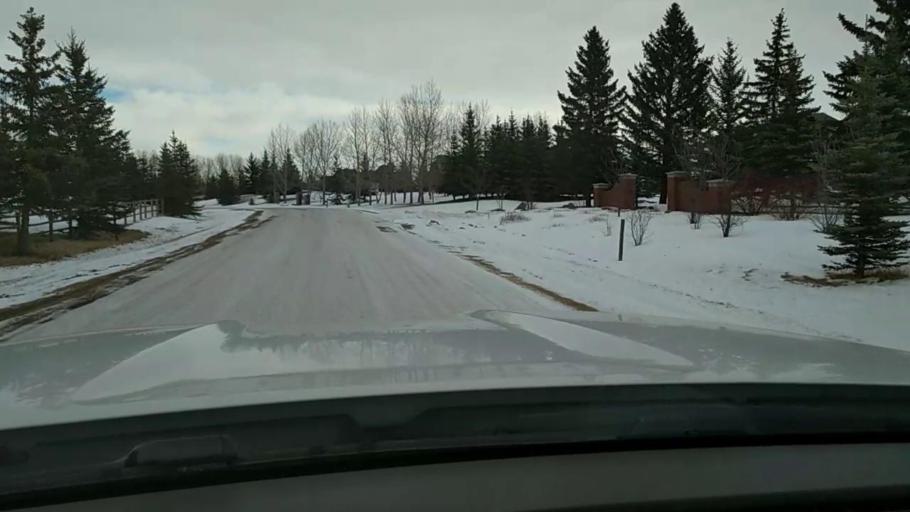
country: CA
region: Alberta
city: Cochrane
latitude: 51.2080
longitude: -114.2855
